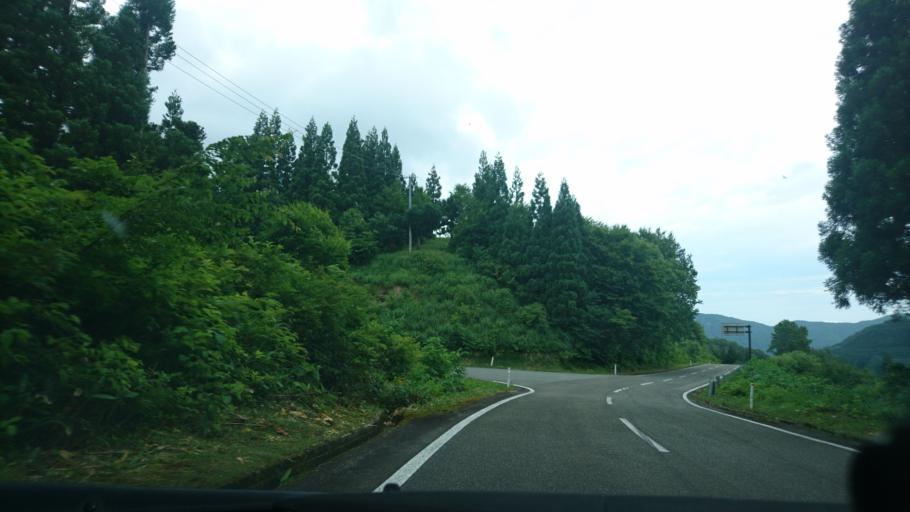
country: JP
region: Akita
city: Yuzawa
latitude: 39.1585
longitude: 140.7496
